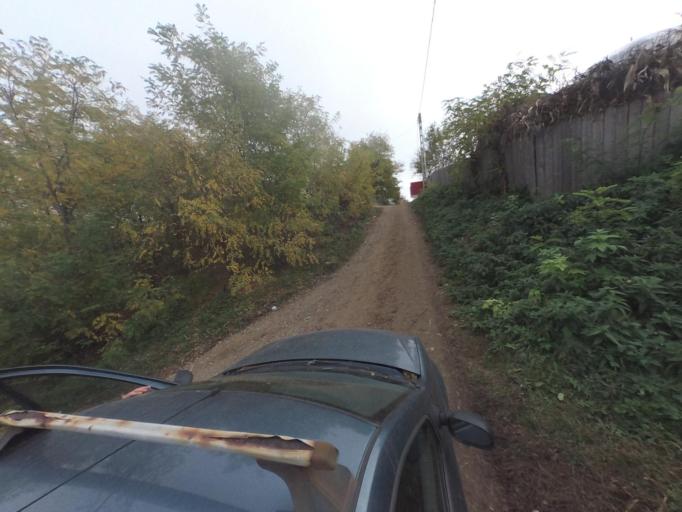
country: RO
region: Vaslui
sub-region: Comuna Bacesti
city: Bacesti
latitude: 46.8341
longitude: 27.2287
